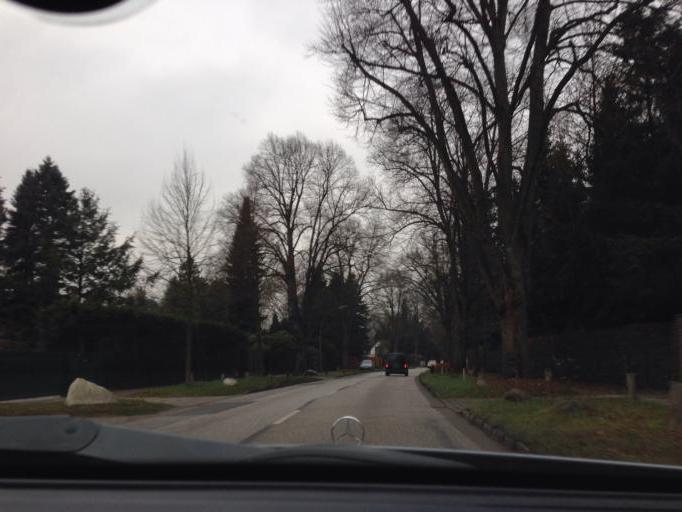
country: DE
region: Hamburg
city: Wohldorf-Ohlstedt
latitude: 53.6996
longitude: 10.1232
